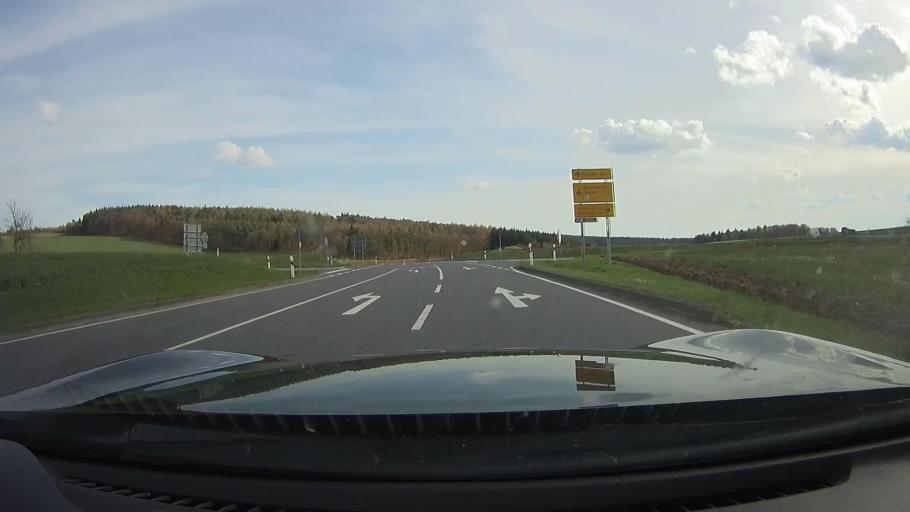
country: DE
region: Baden-Wuerttemberg
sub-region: Karlsruhe Region
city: Walldurn
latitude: 49.6259
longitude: 9.3266
